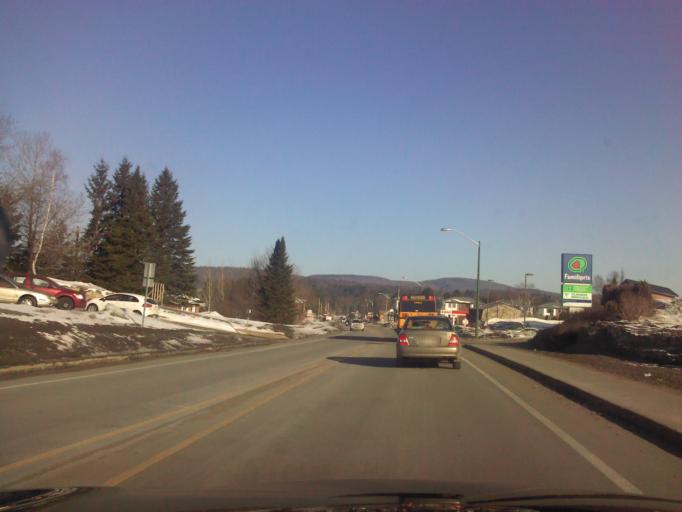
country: CA
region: Quebec
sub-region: Capitale-Nationale
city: Sainte Catherine de la Jacques Cartier
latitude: 46.8410
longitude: -71.6104
